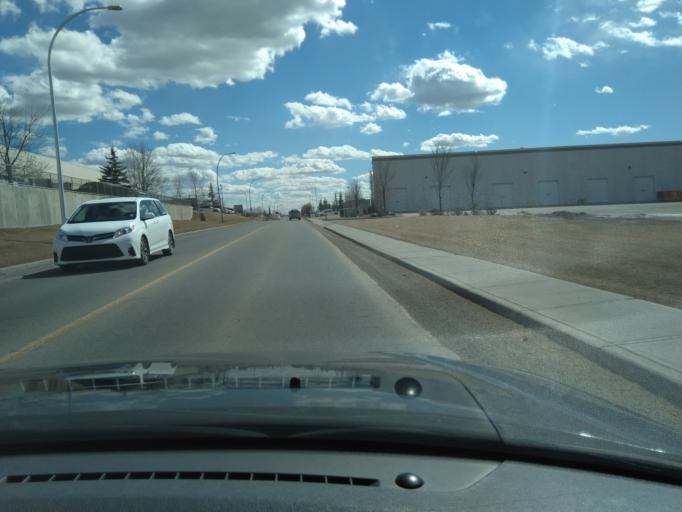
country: CA
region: Alberta
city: Calgary
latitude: 51.1226
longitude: -114.0384
